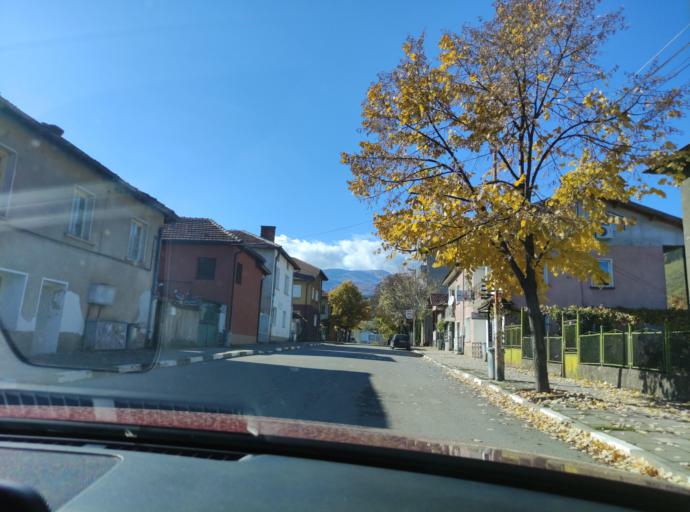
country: BG
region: Montana
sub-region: Obshtina Chiprovtsi
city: Chiprovtsi
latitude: 43.3846
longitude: 22.8839
